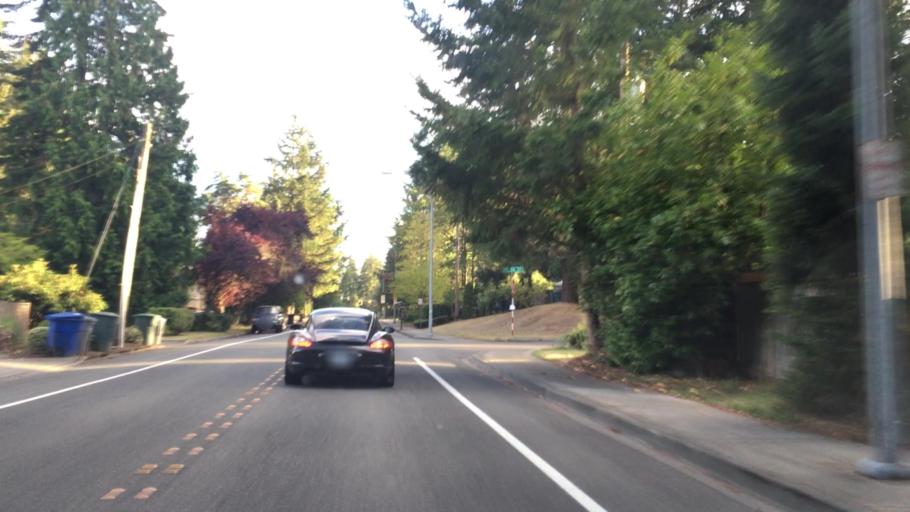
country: US
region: Washington
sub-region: King County
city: Redmond
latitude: 47.6336
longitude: -122.1217
